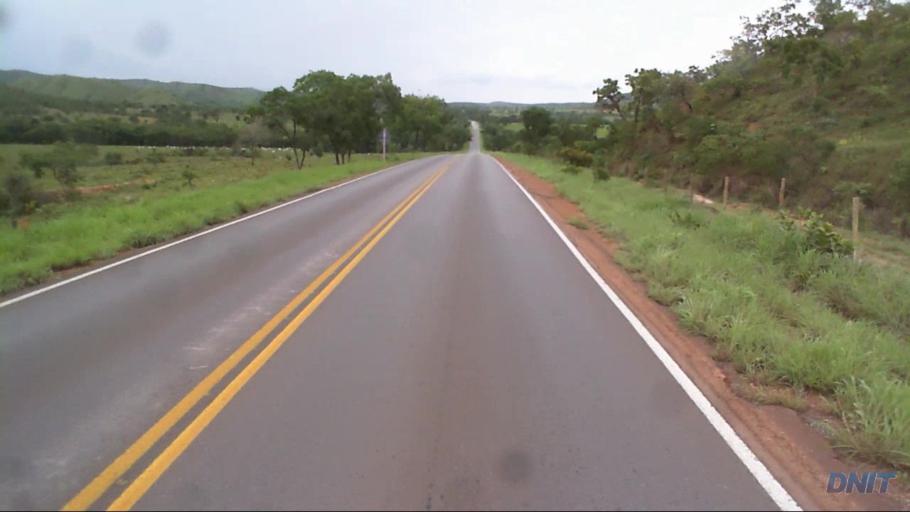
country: BR
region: Goias
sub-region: Padre Bernardo
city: Padre Bernardo
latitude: -15.4399
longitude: -48.1953
